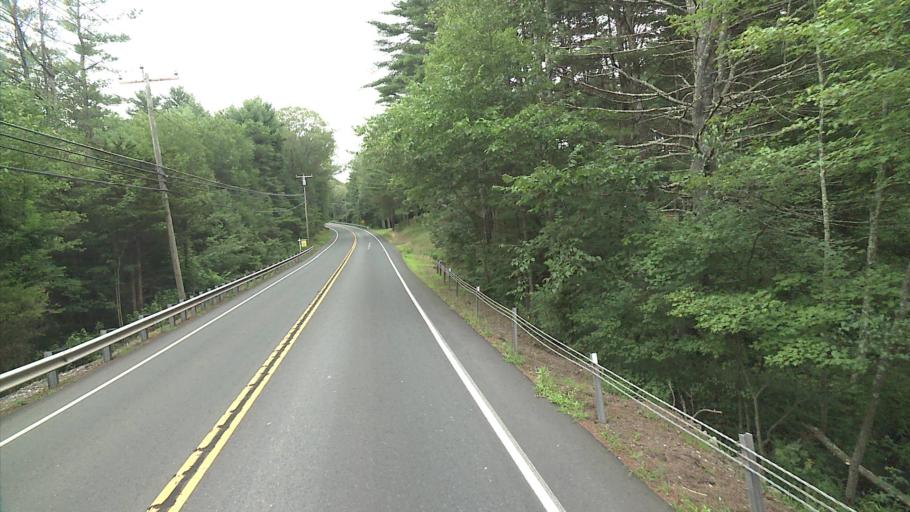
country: US
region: Connecticut
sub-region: Tolland County
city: Tolland
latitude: 41.8841
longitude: -72.3383
